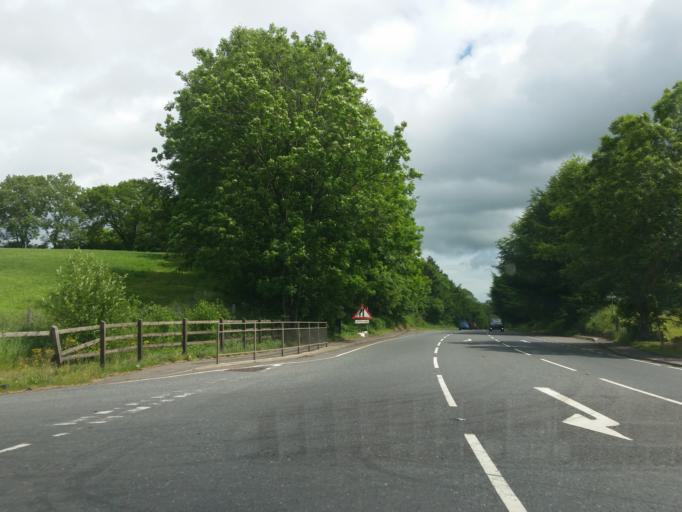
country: IE
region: Ulster
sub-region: County Monaghan
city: Monaghan
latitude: 54.4724
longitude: -7.0537
